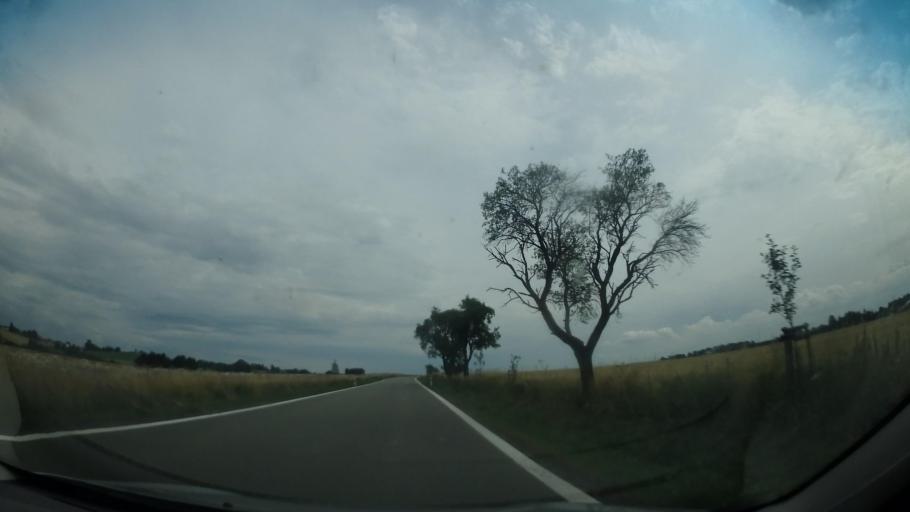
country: CZ
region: Vysocina
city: Bystrice nad Pernstejnem
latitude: 49.4679
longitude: 16.2144
